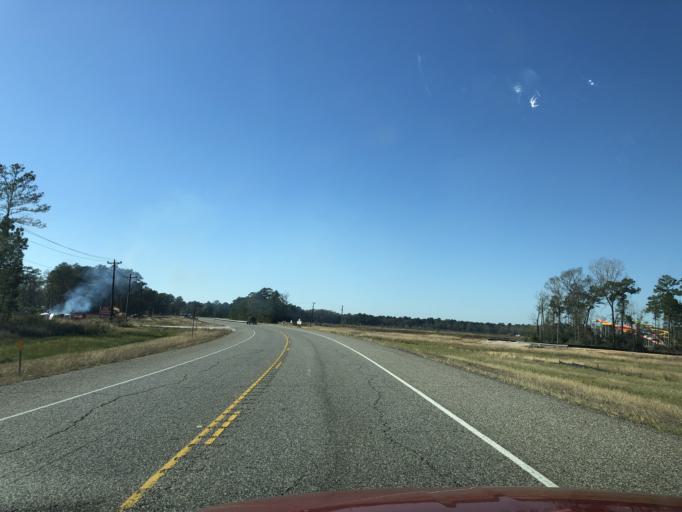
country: US
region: Texas
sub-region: Montgomery County
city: Woodbranch
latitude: 30.1942
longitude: -95.1958
